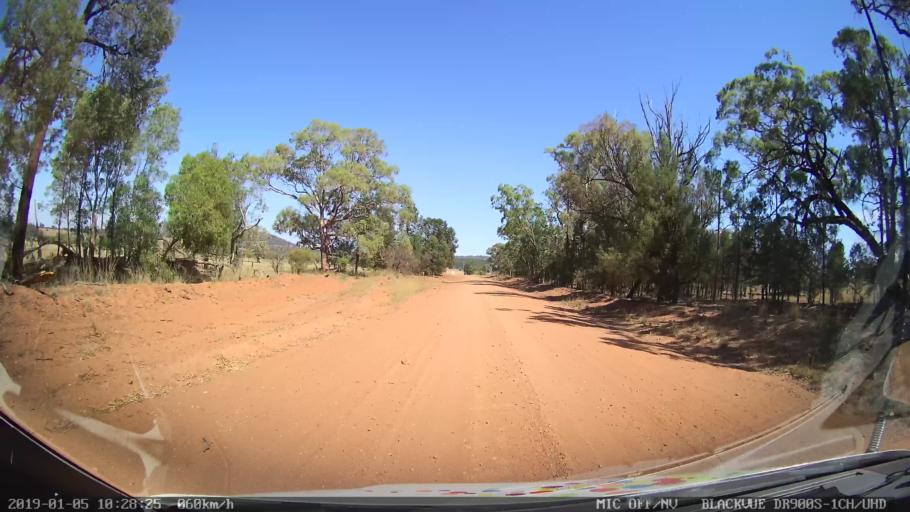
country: AU
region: New South Wales
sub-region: Gilgandra
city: Gilgandra
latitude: -31.5452
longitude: 148.9388
